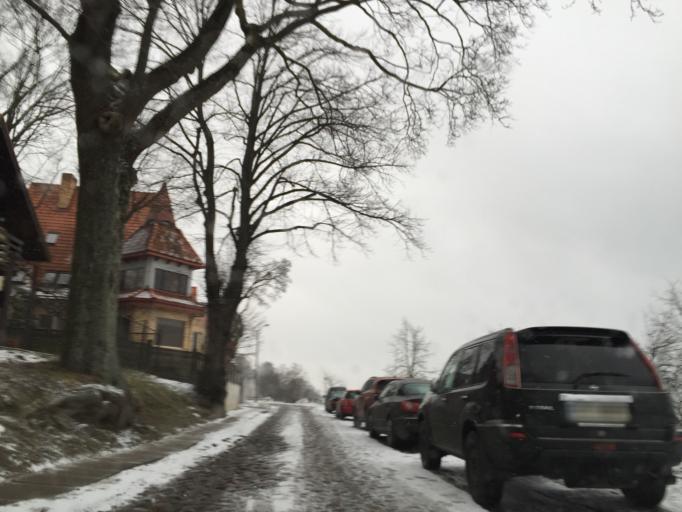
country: LV
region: Riga
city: Riga
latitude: 56.9523
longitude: 24.0864
